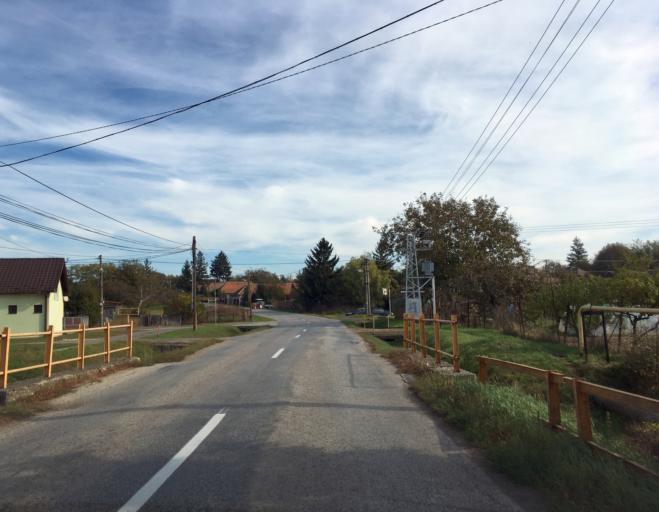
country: SK
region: Nitriansky
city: Svodin
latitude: 47.9864
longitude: 18.4002
